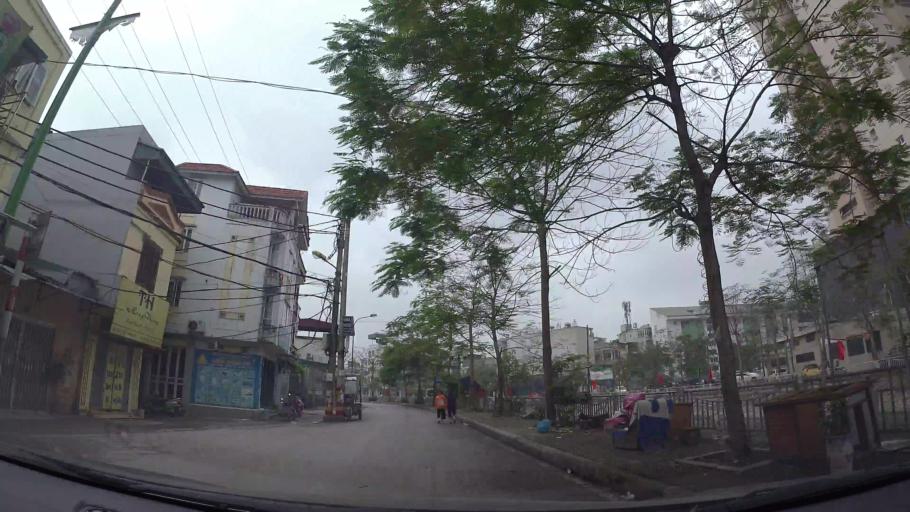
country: VN
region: Ha Noi
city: Van Dien
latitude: 20.9795
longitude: 105.8458
